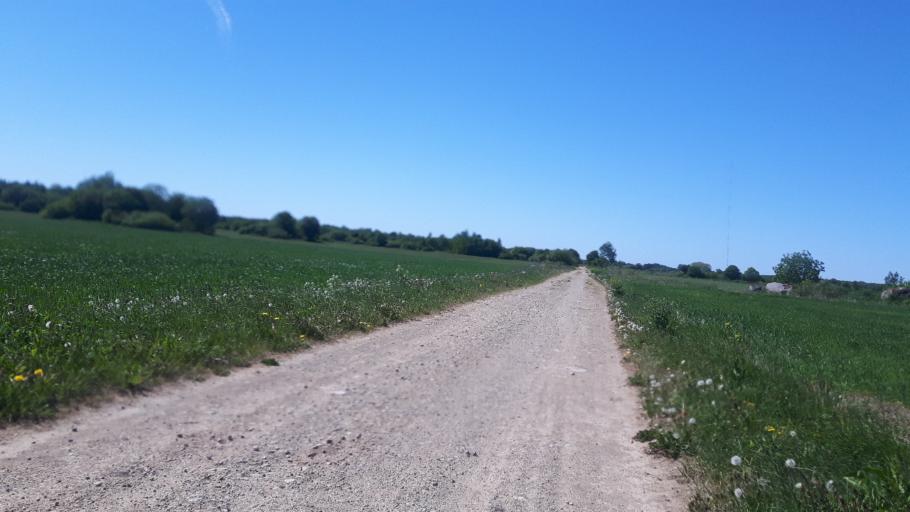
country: EE
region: Ida-Virumaa
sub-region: Toila vald
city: Voka
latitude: 59.4038
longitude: 27.6531
